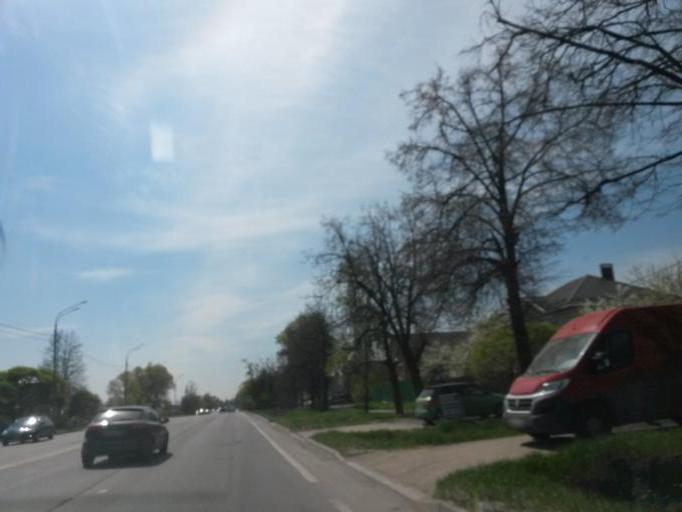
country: RU
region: Moskovskaya
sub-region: Podol'skiy Rayon
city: Podol'sk
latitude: 55.3949
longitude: 37.5469
